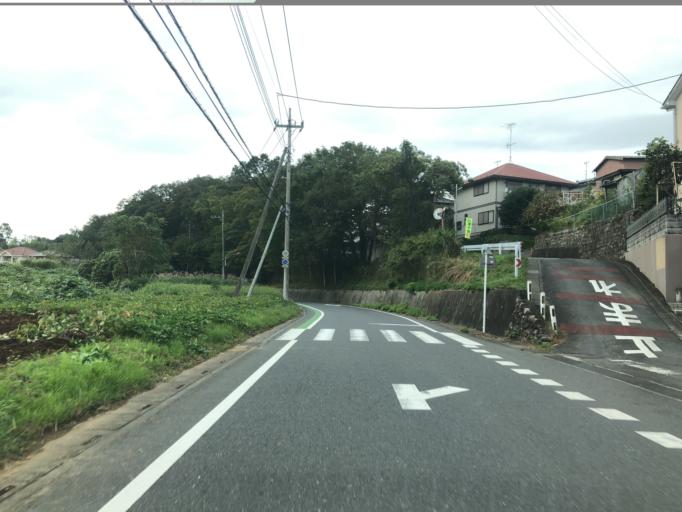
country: JP
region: Saitama
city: Fukiage-fujimi
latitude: 36.0539
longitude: 139.4030
